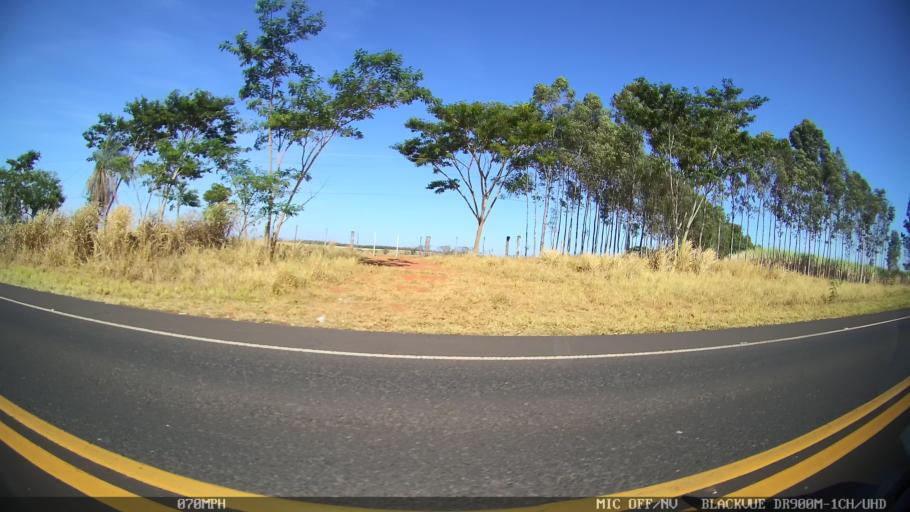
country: BR
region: Sao Paulo
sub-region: Olimpia
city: Olimpia
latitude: -20.6220
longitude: -48.7697
